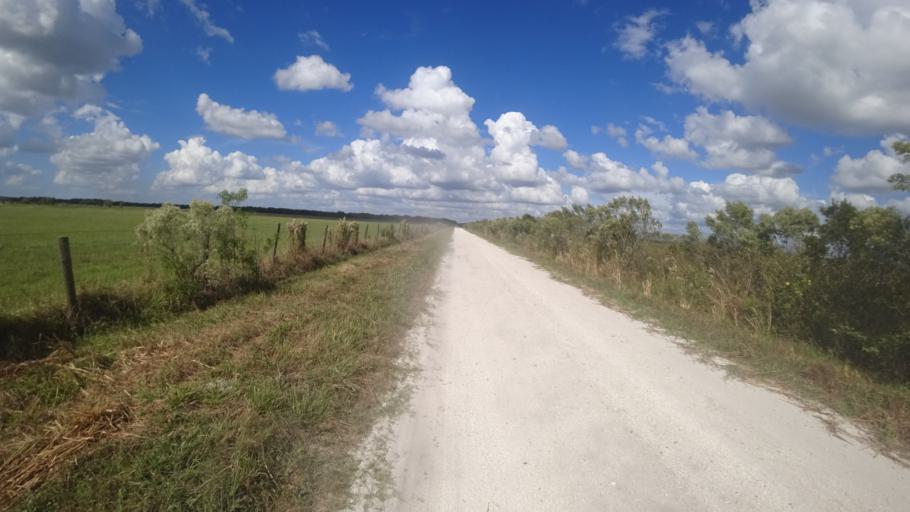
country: US
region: Florida
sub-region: DeSoto County
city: Arcadia
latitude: 27.3226
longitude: -82.1051
